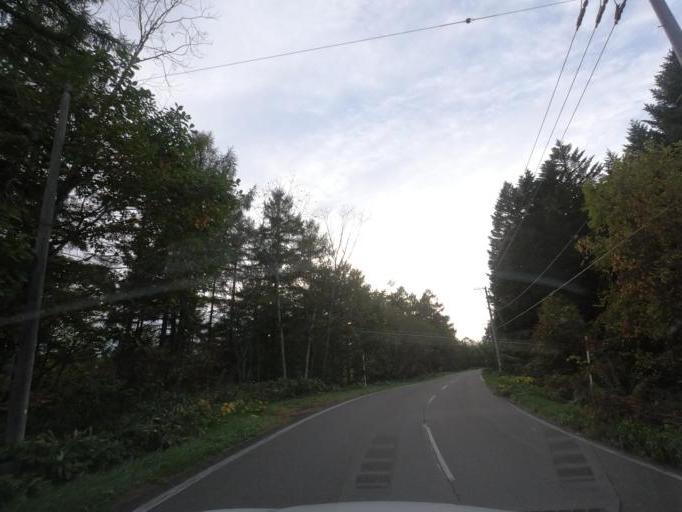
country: JP
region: Hokkaido
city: Obihiro
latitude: 42.5434
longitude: 143.4164
